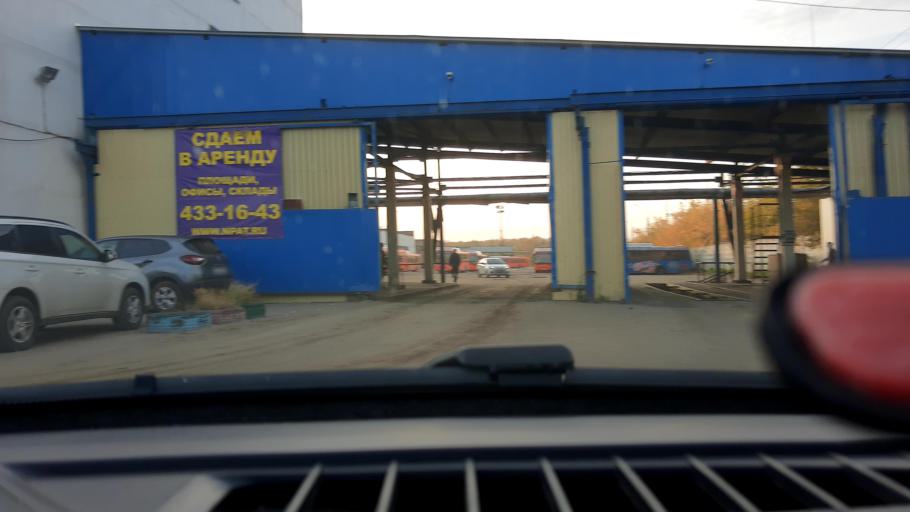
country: RU
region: Nizjnij Novgorod
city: Gorbatovka
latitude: 56.2904
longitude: 43.8722
